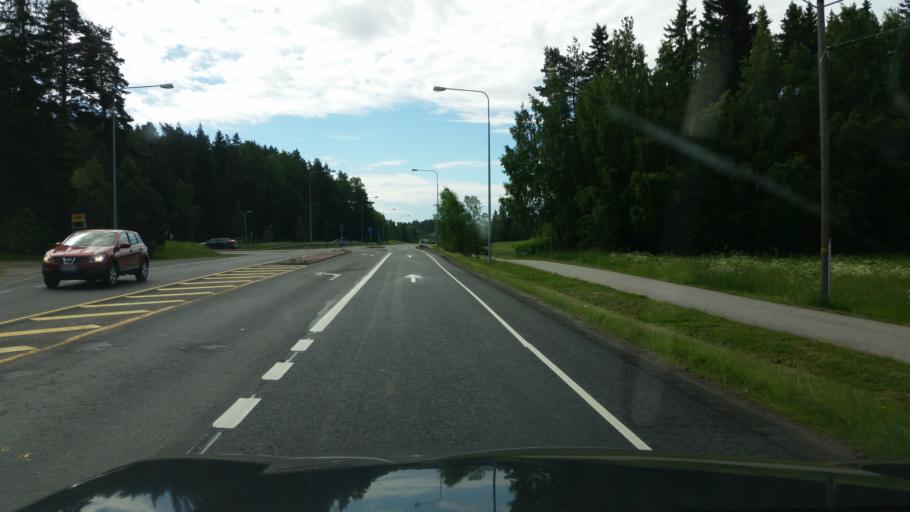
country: FI
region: Varsinais-Suomi
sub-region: Turku
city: Kaarina
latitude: 60.4141
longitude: 22.3839
